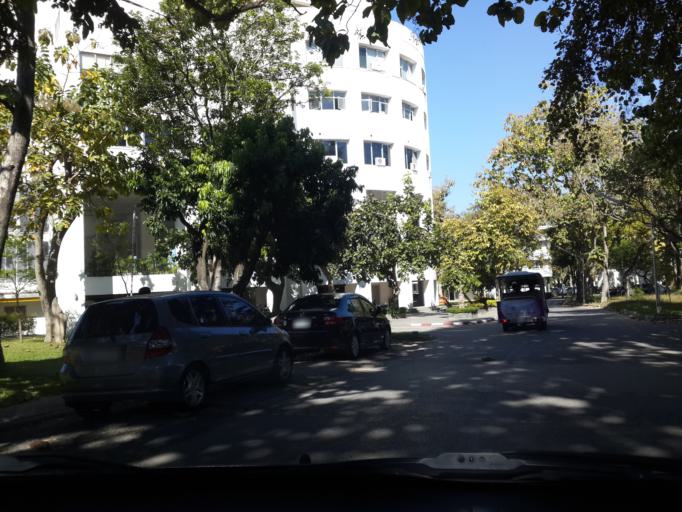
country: TH
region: Chiang Mai
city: Chiang Mai
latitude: 18.8008
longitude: 98.9560
